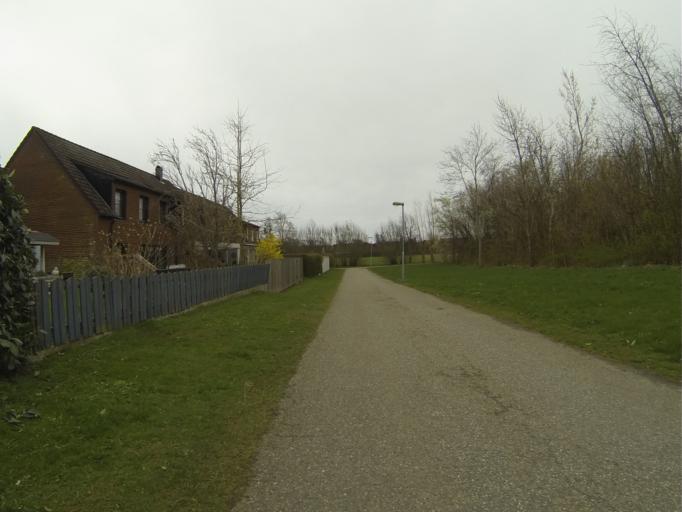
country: SE
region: Skane
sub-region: Simrishamns Kommun
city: Simrishamn
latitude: 55.5443
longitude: 14.3439
